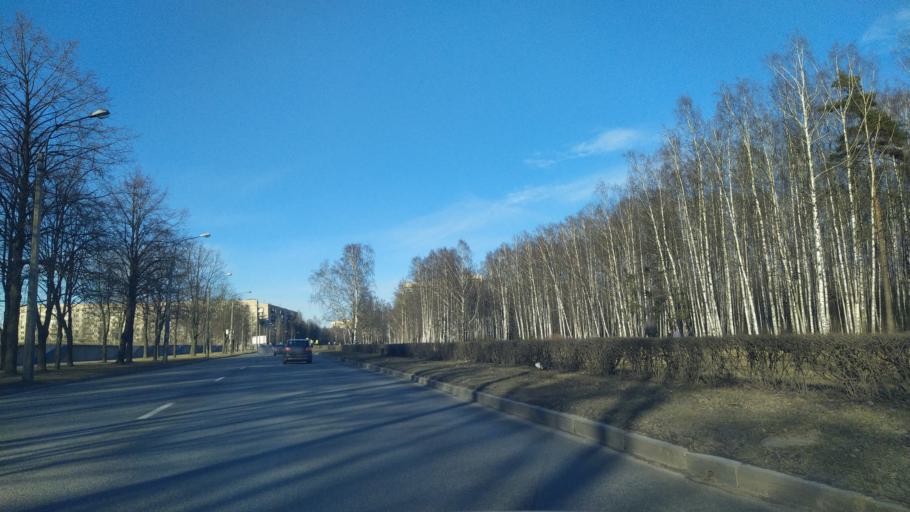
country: RU
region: Leningrad
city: Kalininskiy
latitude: 59.9968
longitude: 30.3926
